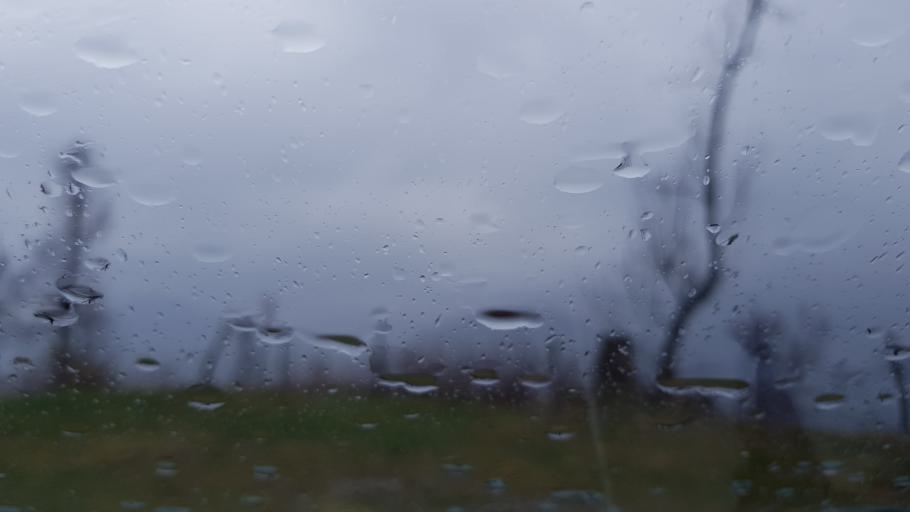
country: SI
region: Cerkno
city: Cerkno
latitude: 46.1430
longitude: 13.8671
